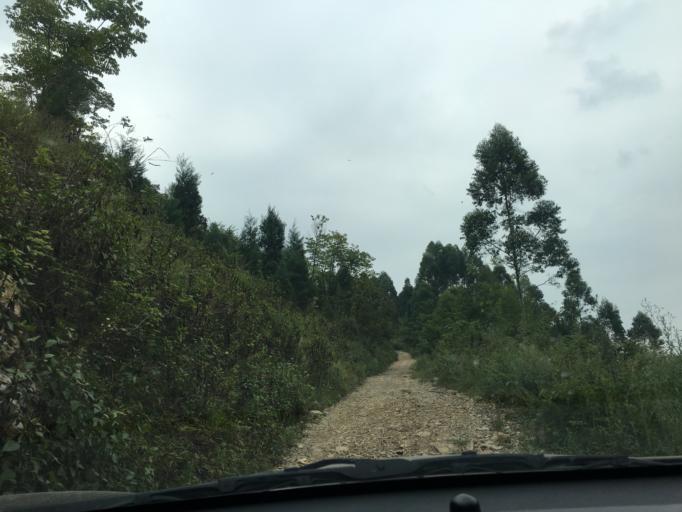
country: CN
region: Guangxi Zhuangzu Zizhiqu
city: Xinzhou
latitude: 25.3790
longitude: 105.6372
